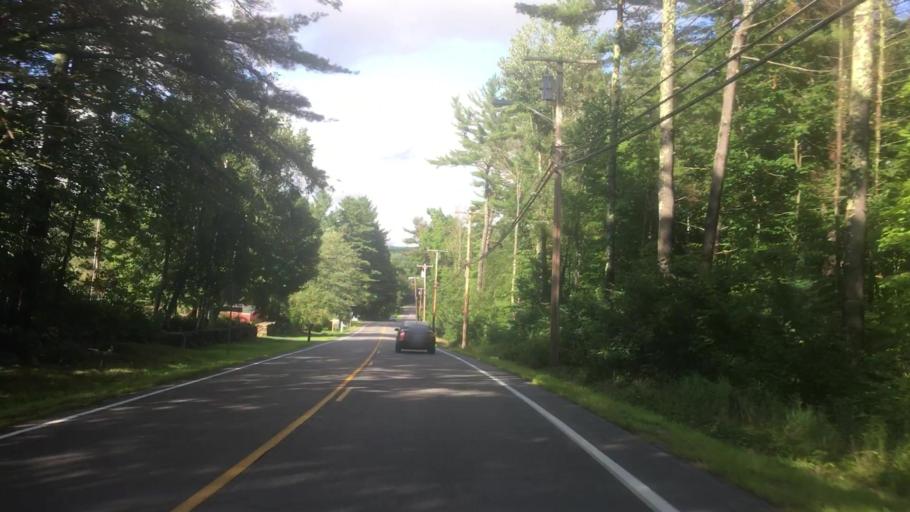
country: US
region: New Hampshire
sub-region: Merrimack County
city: Hopkinton
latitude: 43.1909
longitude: -71.6080
